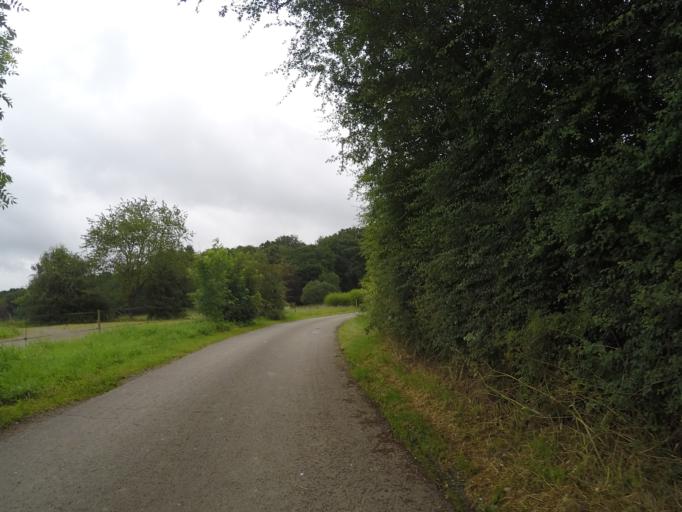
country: BE
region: Wallonia
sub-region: Province de Namur
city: Yvoir
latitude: 50.3260
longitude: 4.9261
